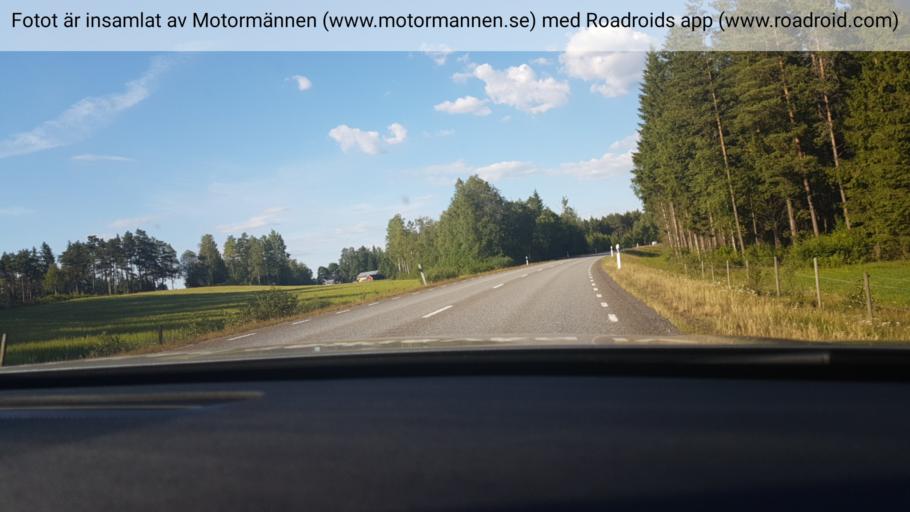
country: SE
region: Joenkoeping
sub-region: Gnosjo Kommun
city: Marieholm
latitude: 57.6517
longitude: 13.8119
